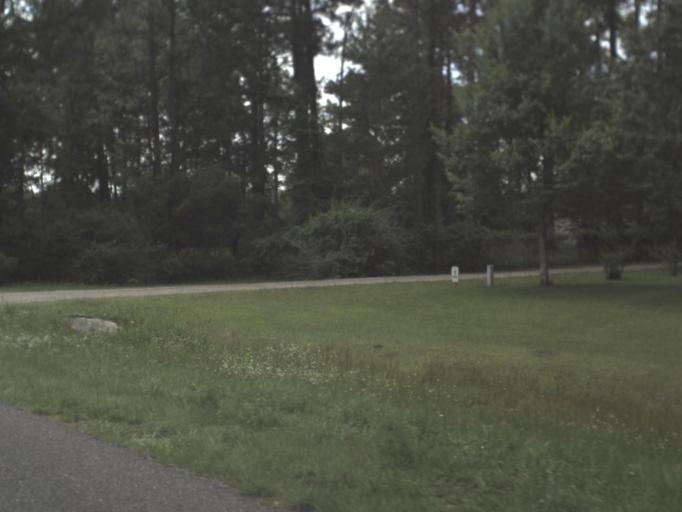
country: US
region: Florida
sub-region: Nassau County
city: Hilliard
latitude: 30.7406
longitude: -81.9525
